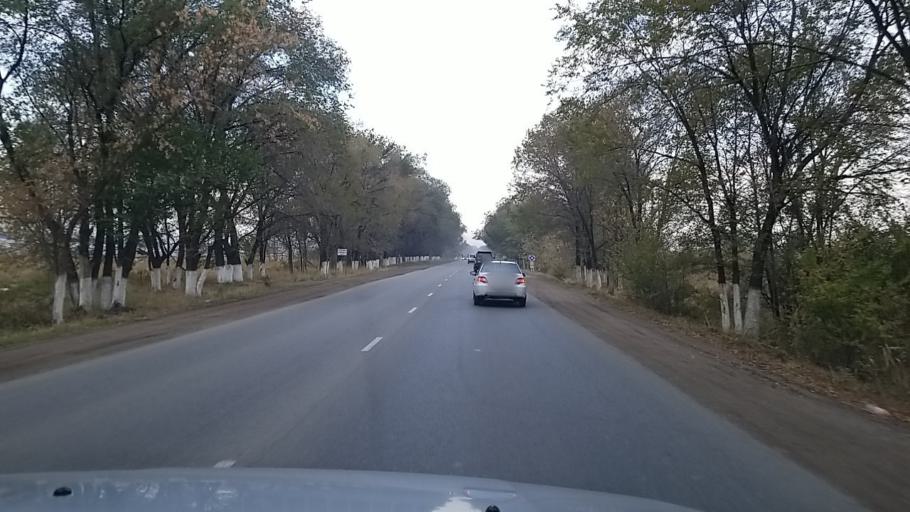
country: KZ
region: Almaty Oblysy
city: Burunday
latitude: 43.3582
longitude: 76.7769
